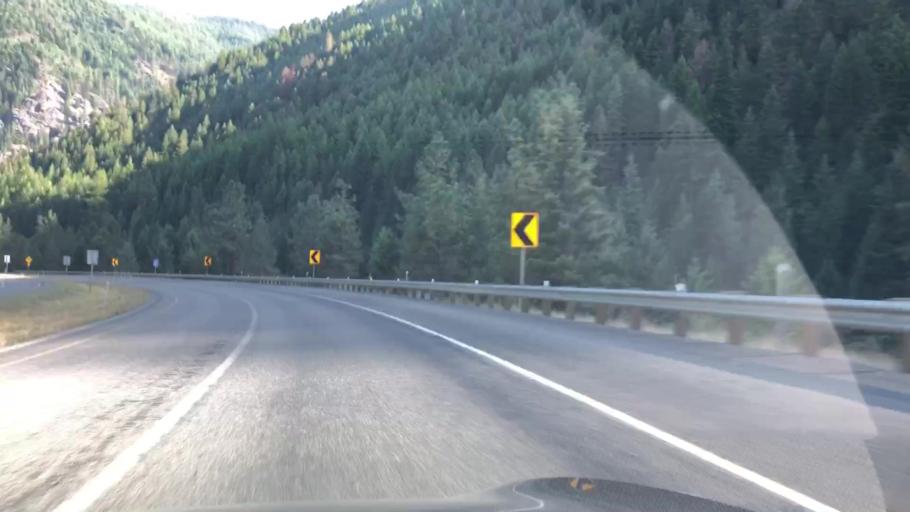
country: US
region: Montana
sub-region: Sanders County
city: Thompson Falls
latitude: 47.3173
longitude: -115.2437
